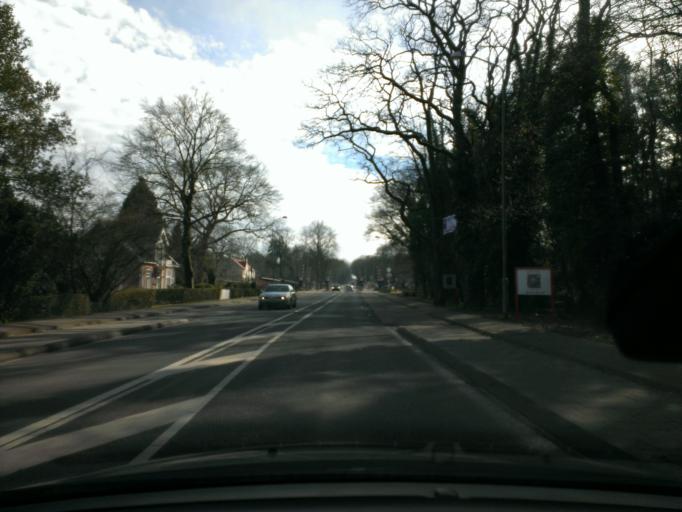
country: NL
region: Gelderland
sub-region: Gemeente Hattem
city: Hattem
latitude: 52.4552
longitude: 6.0016
